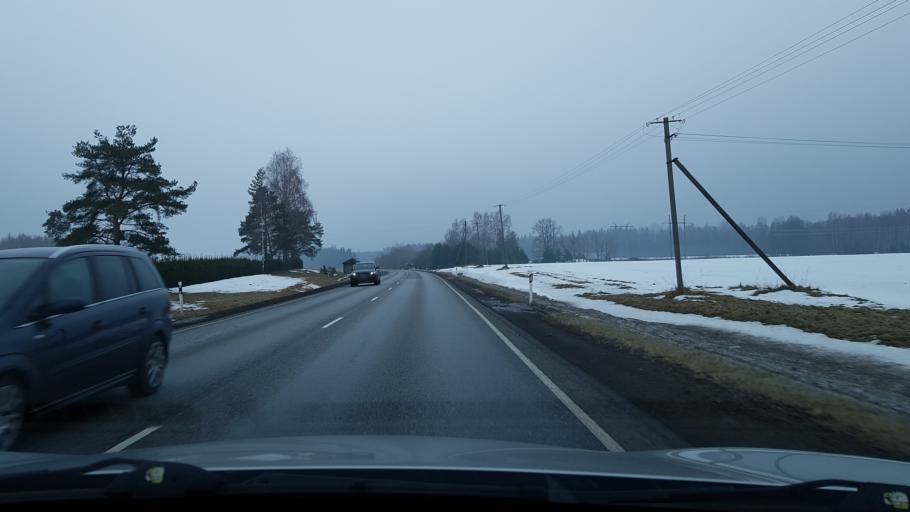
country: EE
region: Valgamaa
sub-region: Valga linn
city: Valga
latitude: 57.9006
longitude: 26.1702
